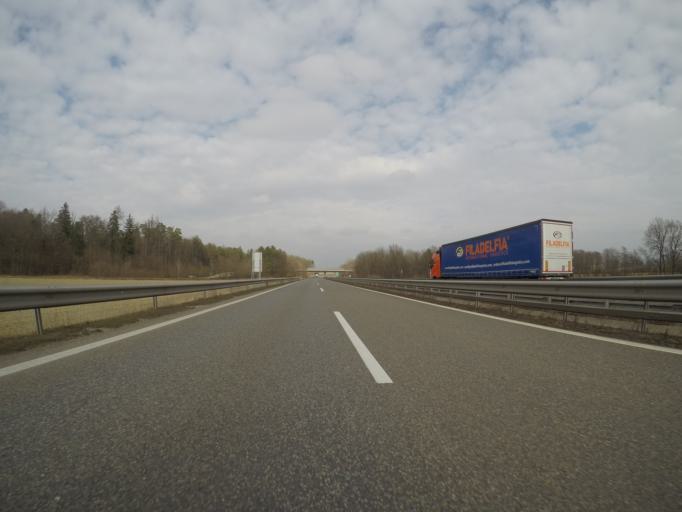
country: SI
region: Krizevci
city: Krizevci pri Ljutomeru
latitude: 46.5830
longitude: 16.0894
